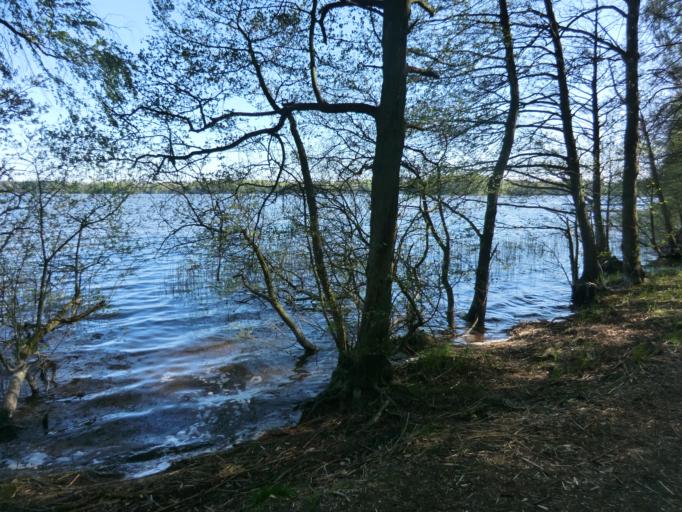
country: SE
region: Skane
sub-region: Sjobo Kommun
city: Sjoebo
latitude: 55.5670
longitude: 13.7183
